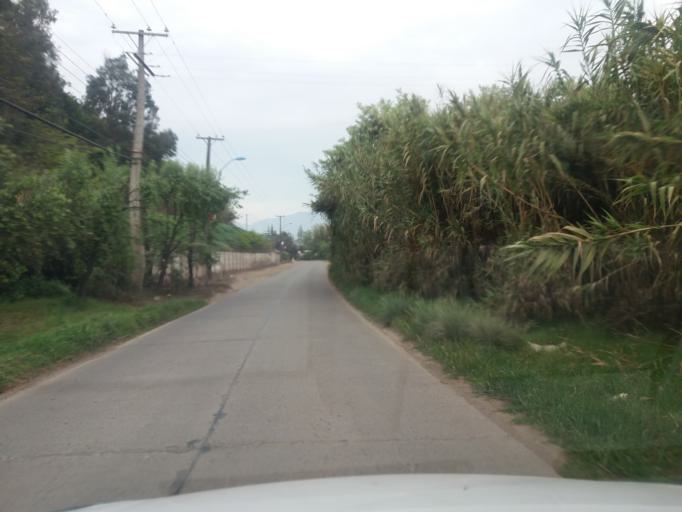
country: CL
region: Valparaiso
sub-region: Provincia de Quillota
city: Hacienda La Calera
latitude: -32.8250
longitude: -71.1286
